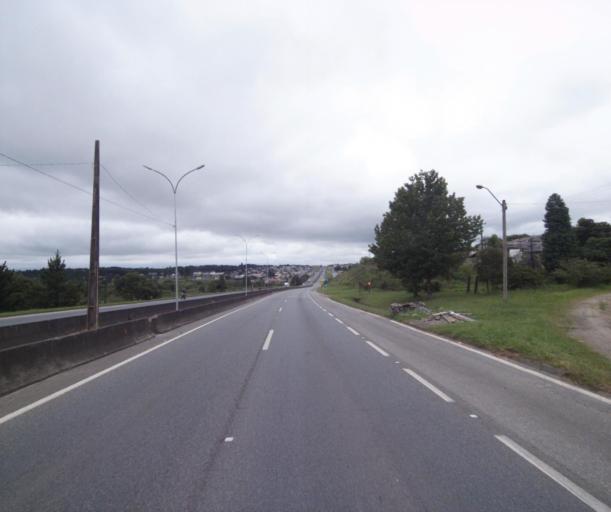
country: BR
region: Parana
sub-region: Quatro Barras
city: Quatro Barras
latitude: -25.3643
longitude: -49.0861
